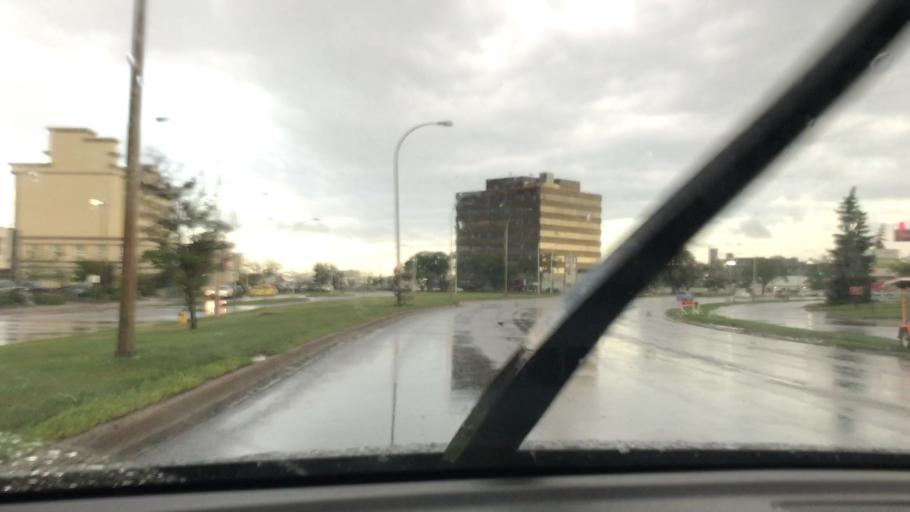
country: CA
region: Alberta
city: Edmonton
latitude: 53.4922
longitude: -113.4960
